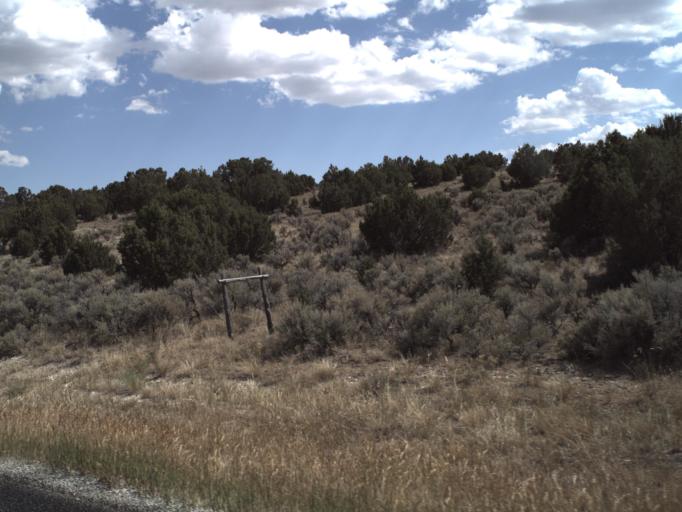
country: US
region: Idaho
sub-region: Minidoka County
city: Rupert
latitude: 41.9843
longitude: -113.1736
